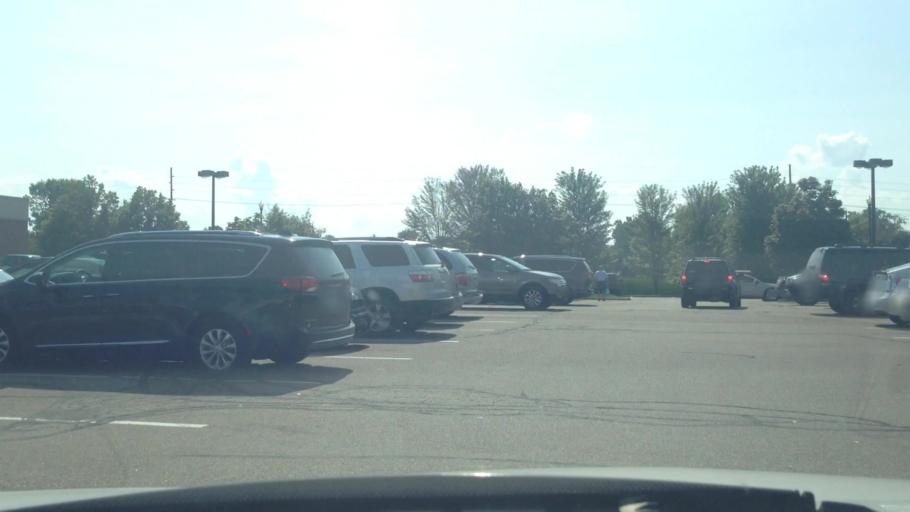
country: US
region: Michigan
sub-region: Oakland County
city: Clarkston
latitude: 42.7221
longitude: -83.3768
